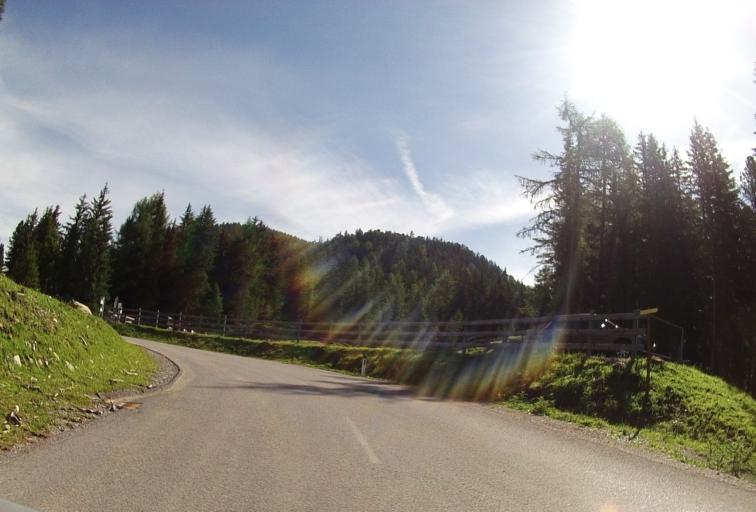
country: AT
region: Tyrol
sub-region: Politischer Bezirk Imst
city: Silz
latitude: 47.2311
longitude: 10.9276
